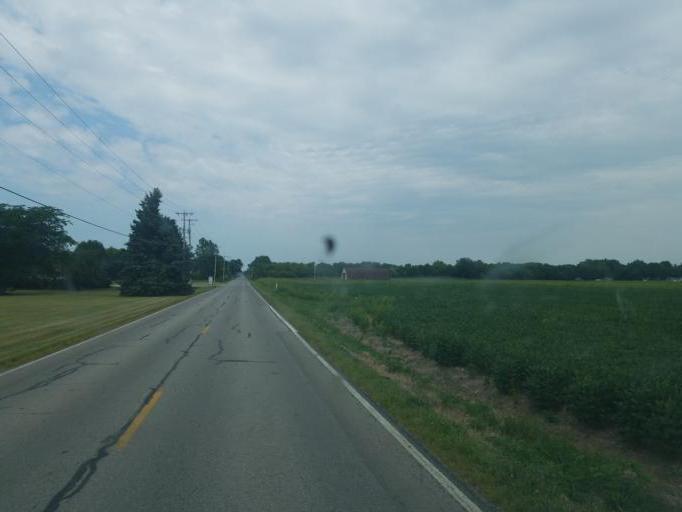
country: US
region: Ohio
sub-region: Marion County
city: Marion
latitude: 40.5664
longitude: -83.1645
